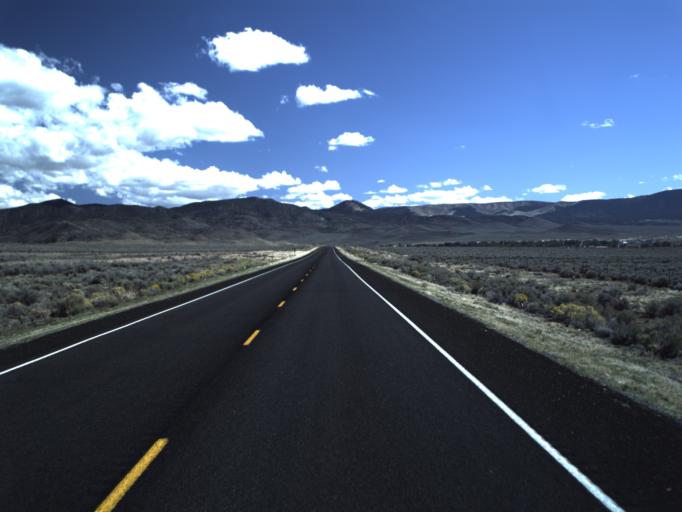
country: US
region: Utah
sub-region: Beaver County
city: Milford
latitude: 38.2465
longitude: -112.9430
